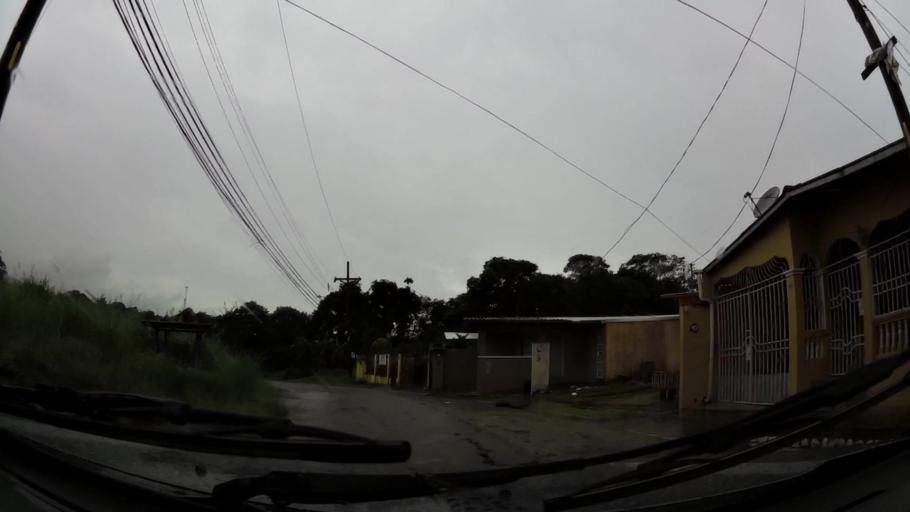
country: PA
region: Colon
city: Puerto Pilon
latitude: 9.3609
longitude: -79.8028
